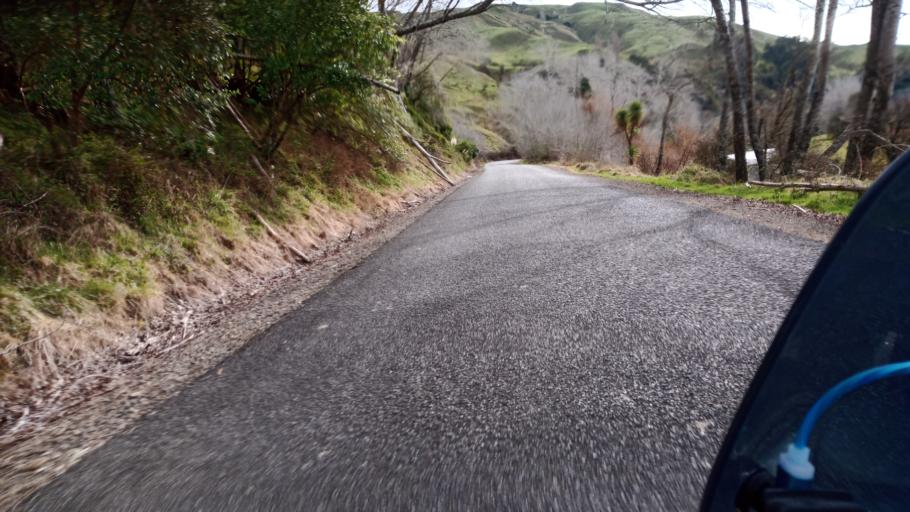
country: NZ
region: Hawke's Bay
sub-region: Wairoa District
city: Wairoa
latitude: -38.7918
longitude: 177.4338
